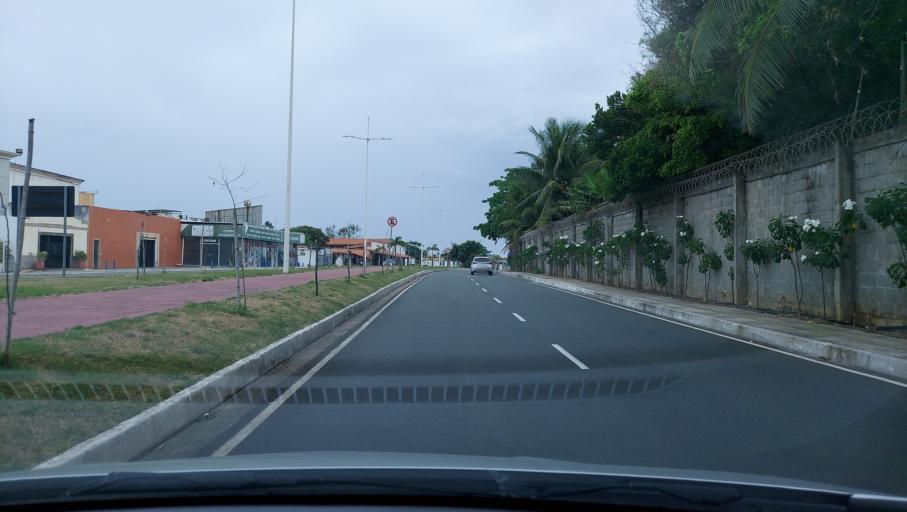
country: BR
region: Bahia
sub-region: Lauro De Freitas
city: Lauro de Freitas
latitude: -12.9580
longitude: -38.4017
